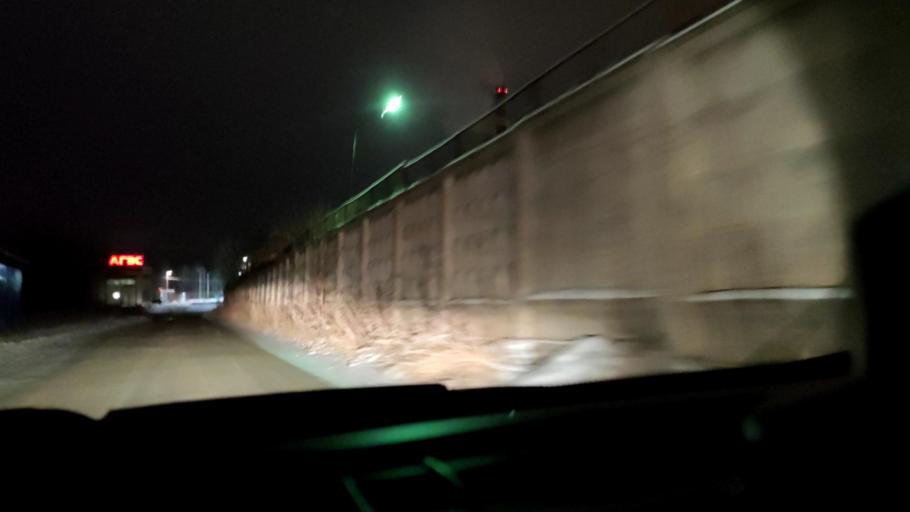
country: RU
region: Perm
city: Perm
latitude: 58.0408
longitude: 56.3152
